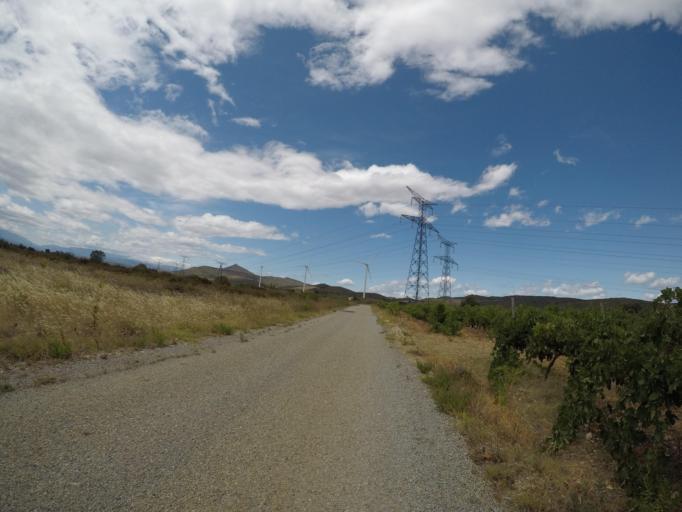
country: FR
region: Languedoc-Roussillon
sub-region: Departement des Pyrenees-Orientales
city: Pezilla-la-Riviere
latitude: 42.7203
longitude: 2.7573
